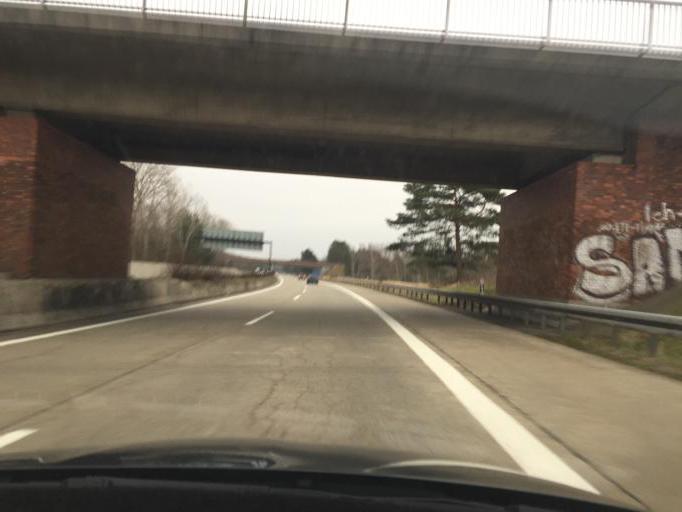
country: DE
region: Brandenburg
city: Lubbenau
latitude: 51.8402
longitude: 13.9367
